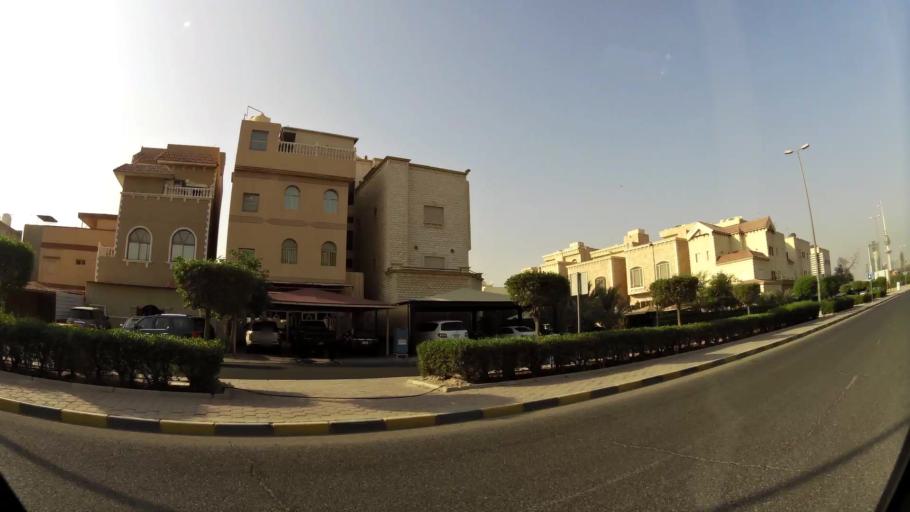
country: KW
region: Al Asimah
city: Ad Dasmah
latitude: 29.3688
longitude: 47.9968
